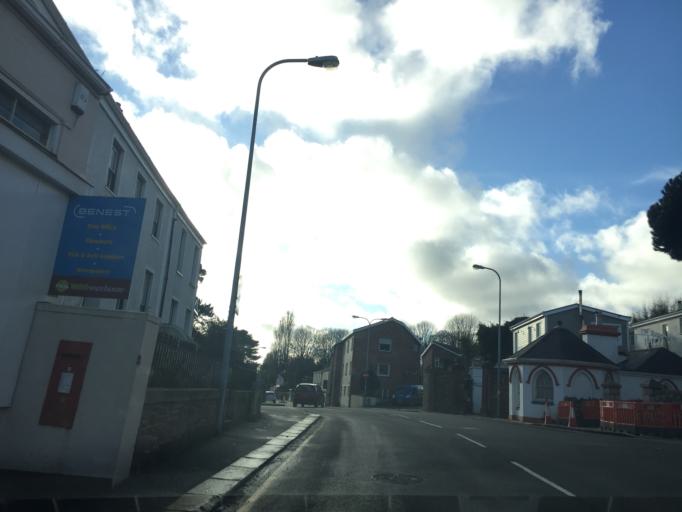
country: JE
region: St Helier
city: Saint Helier
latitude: 49.1985
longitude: -2.1381
